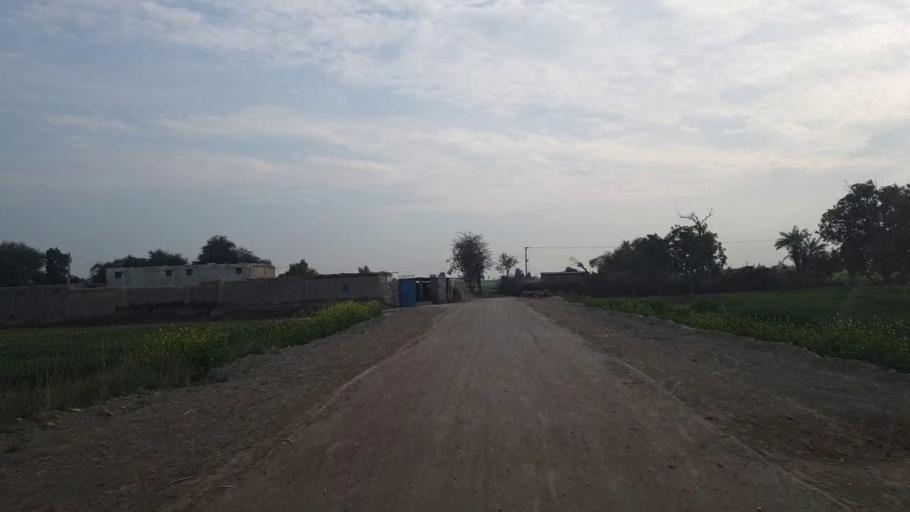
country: PK
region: Sindh
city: Shahpur Chakar
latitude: 26.0625
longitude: 68.5484
